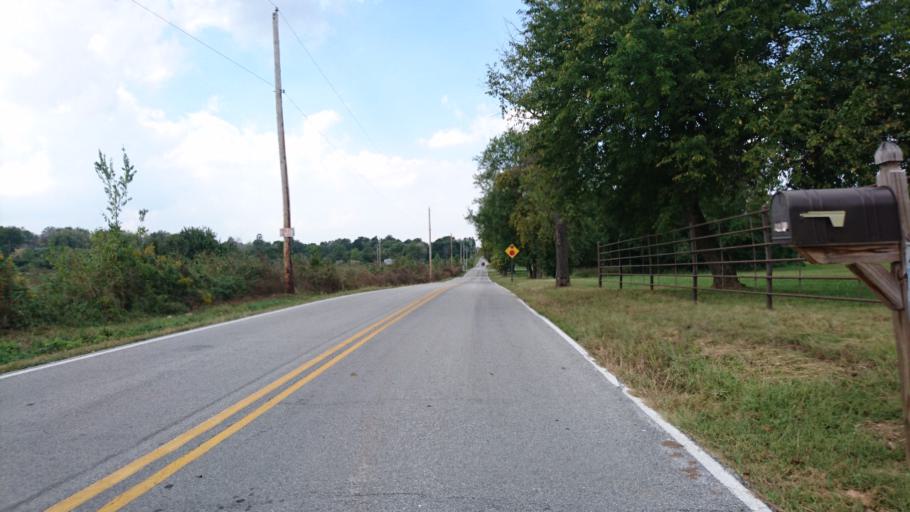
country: US
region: Missouri
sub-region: Greene County
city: Battlefield
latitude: 37.1980
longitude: -93.3839
